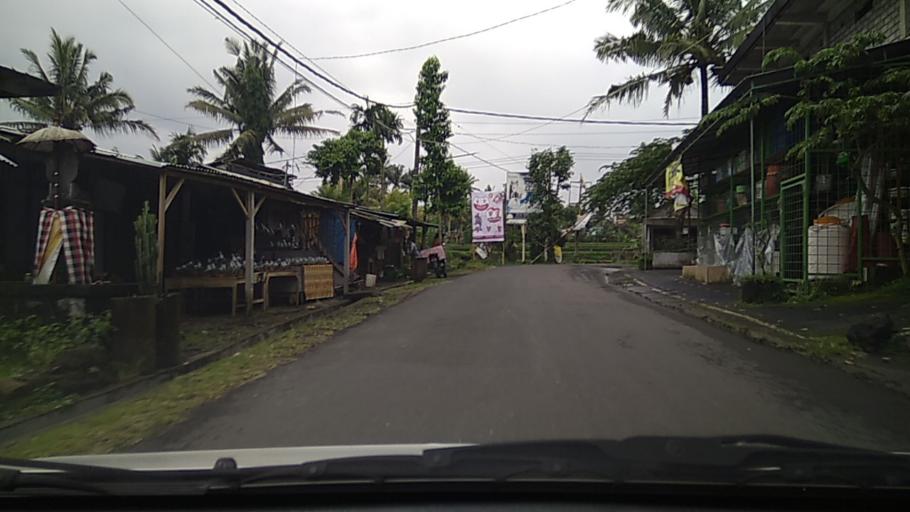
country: ID
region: Bali
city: Banjar Dujung Kaja
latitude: -8.4112
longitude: 115.2916
